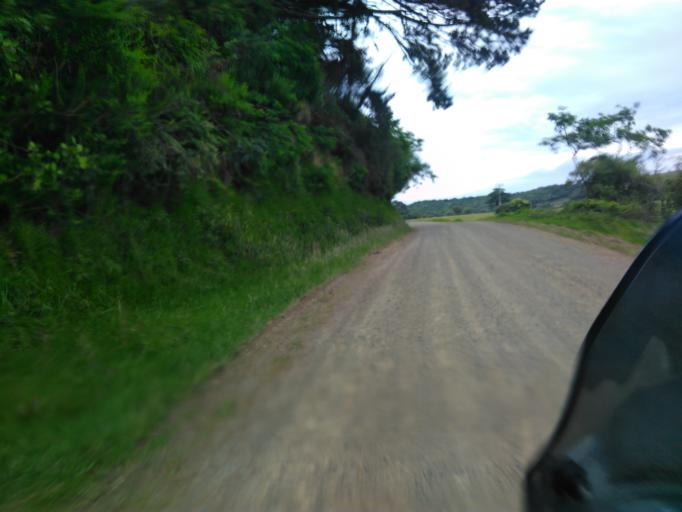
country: NZ
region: Bay of Plenty
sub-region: Opotiki District
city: Opotiki
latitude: -38.0197
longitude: 177.4335
